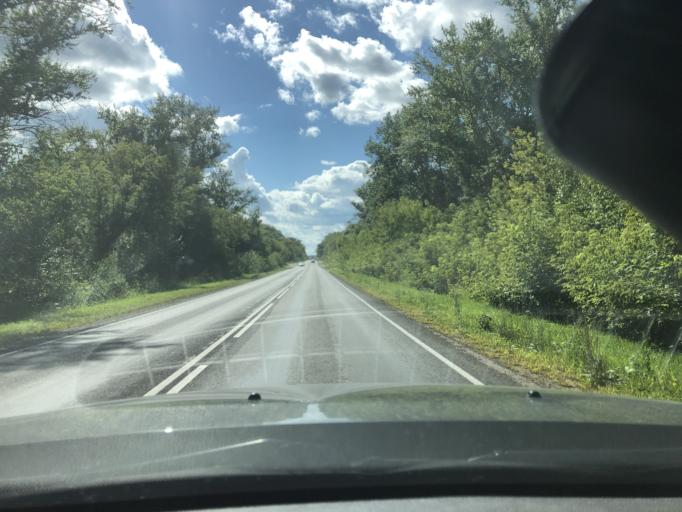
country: RU
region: Tula
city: Kimovsk
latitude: 53.9705
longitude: 38.4695
